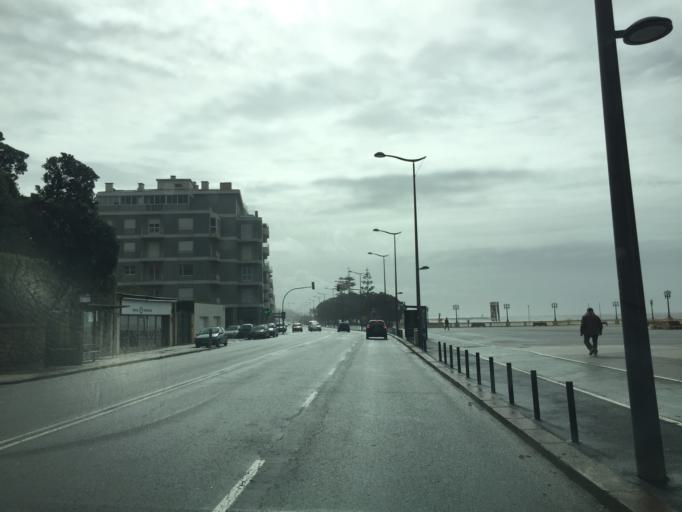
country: PT
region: Porto
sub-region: Matosinhos
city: Matosinhos
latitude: 41.1600
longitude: -8.6841
